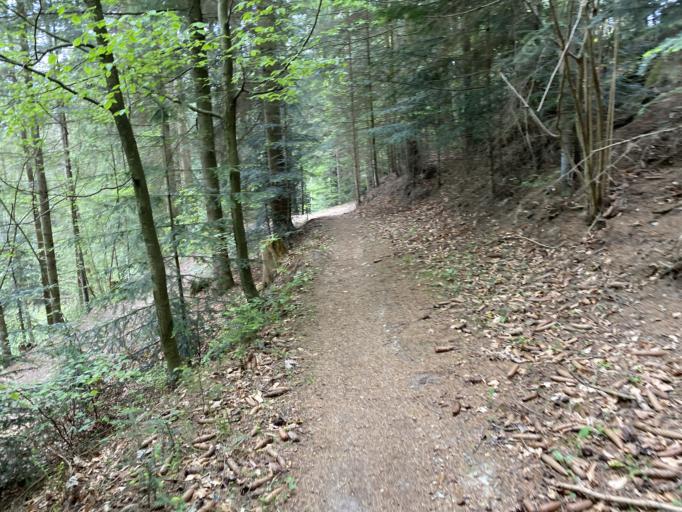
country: AT
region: Styria
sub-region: Politischer Bezirk Weiz
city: Birkfeld
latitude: 47.3515
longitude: 15.7075
